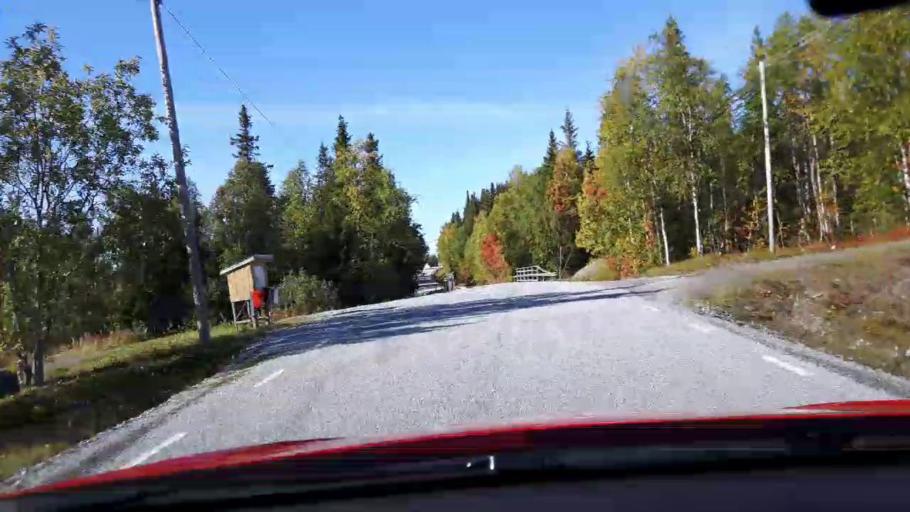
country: NO
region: Nord-Trondelag
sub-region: Royrvik
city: Royrvik
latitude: 64.8277
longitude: 14.1245
